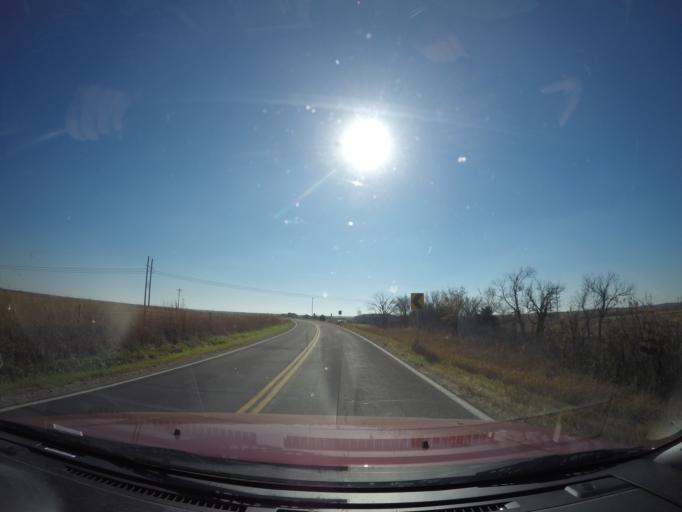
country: US
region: Kansas
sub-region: Geary County
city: Grandview Plaza
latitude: 39.0185
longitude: -96.7614
